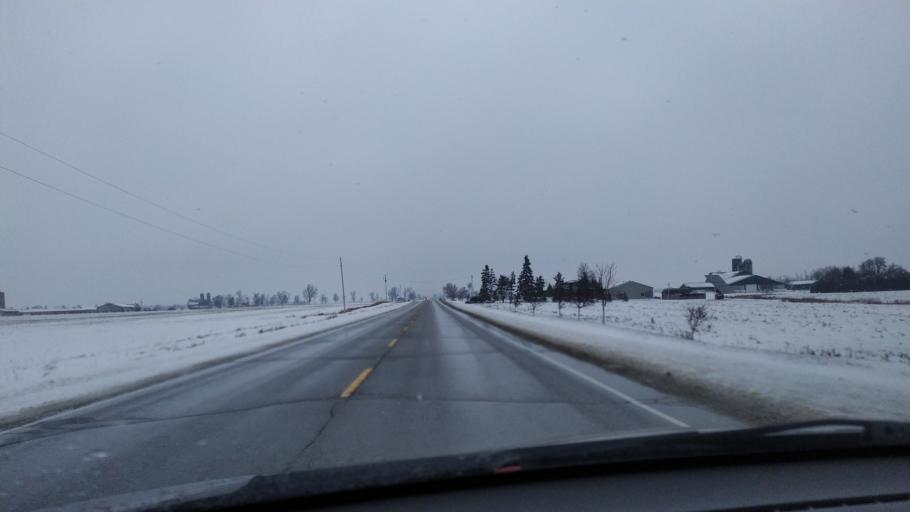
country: CA
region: Ontario
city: Stratford
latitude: 43.5389
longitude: -80.8649
